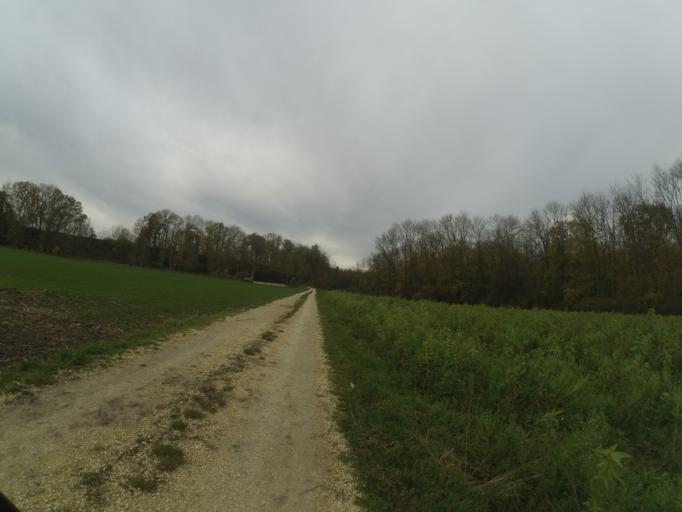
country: DE
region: Bavaria
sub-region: Swabia
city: Senden
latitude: 48.3429
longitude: 10.0046
